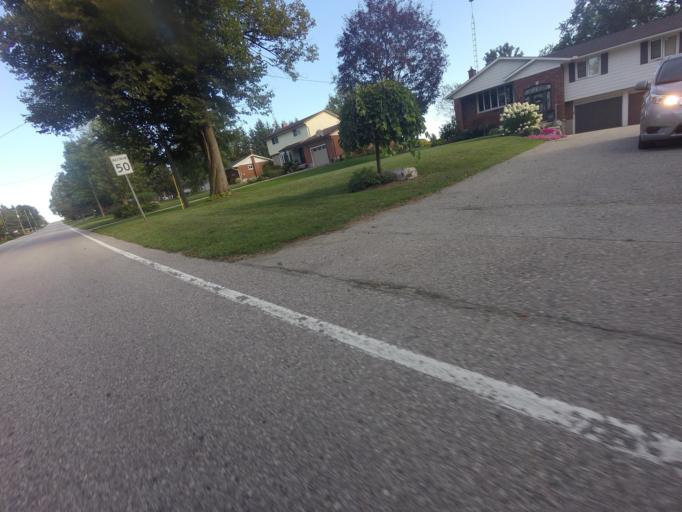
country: CA
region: Ontario
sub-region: Wellington County
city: Guelph
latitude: 43.5985
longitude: -80.3437
